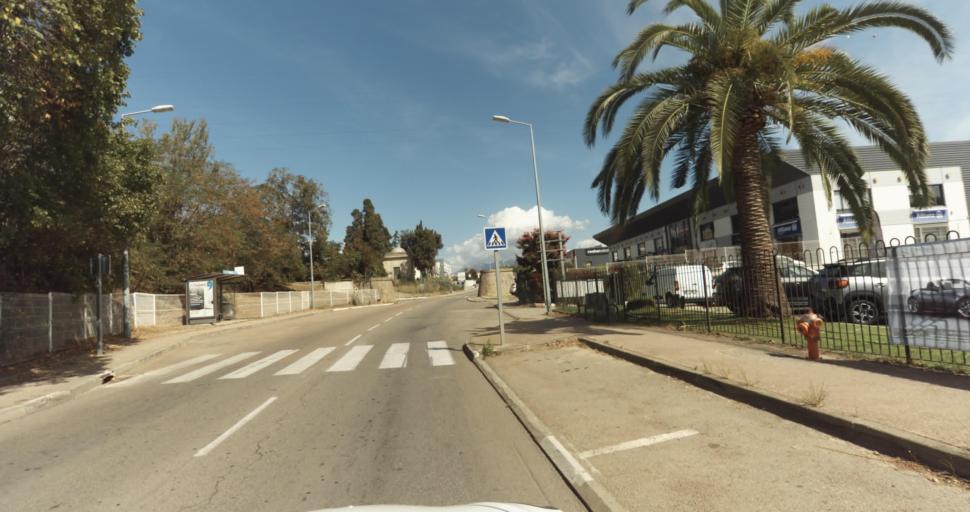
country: FR
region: Corsica
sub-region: Departement de la Corse-du-Sud
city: Ajaccio
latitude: 41.9473
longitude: 8.7628
